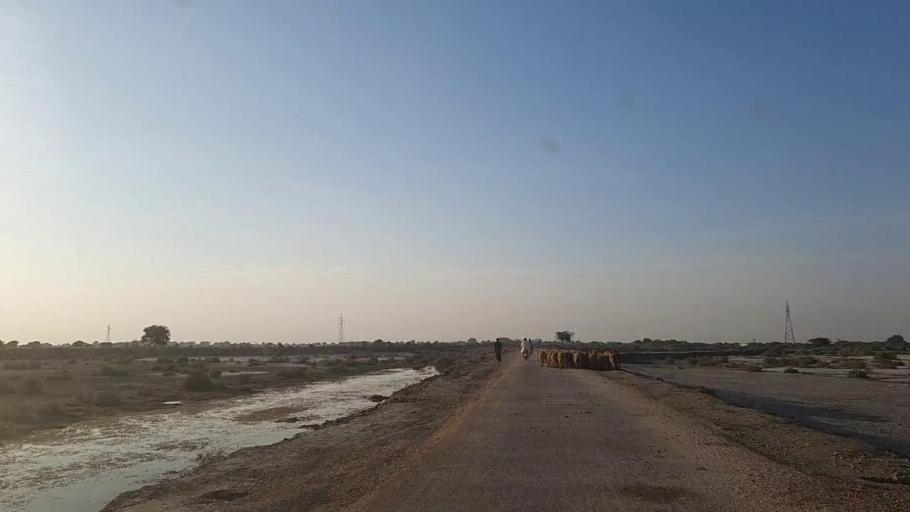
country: PK
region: Sindh
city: Mirpur Batoro
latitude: 24.6904
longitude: 68.2023
